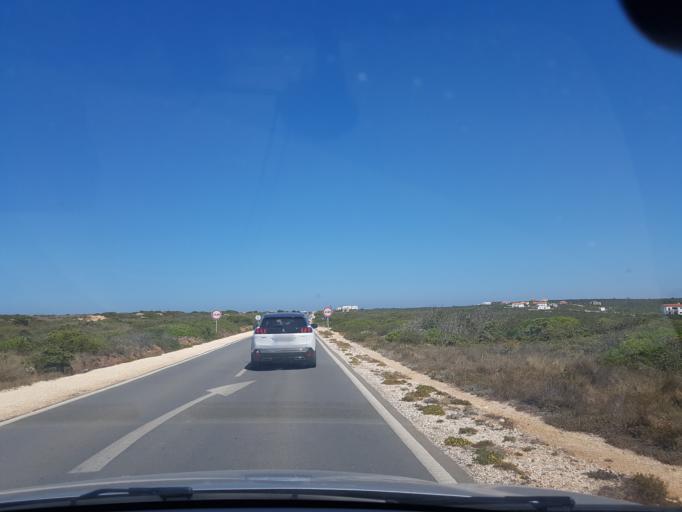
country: PT
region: Faro
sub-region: Vila do Bispo
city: Sagres
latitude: 37.0169
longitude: -8.9548
